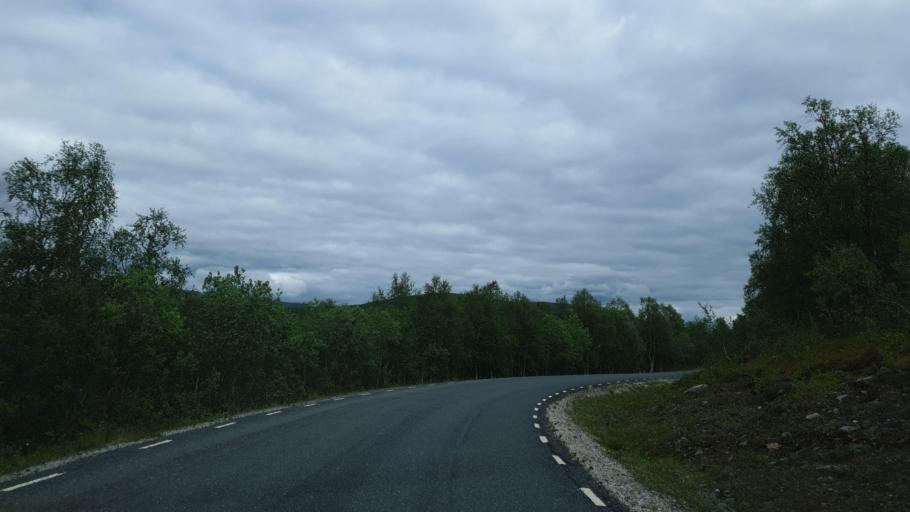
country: NO
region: Nordland
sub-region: Hattfjelldal
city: Hattfjelldal
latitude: 65.4237
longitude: 14.9043
